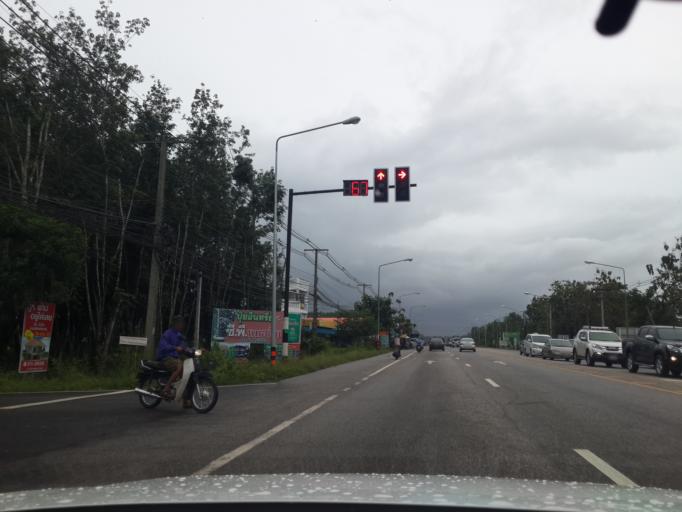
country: TH
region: Songkhla
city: Khlong Hoi Khong
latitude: 6.9587
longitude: 100.4226
